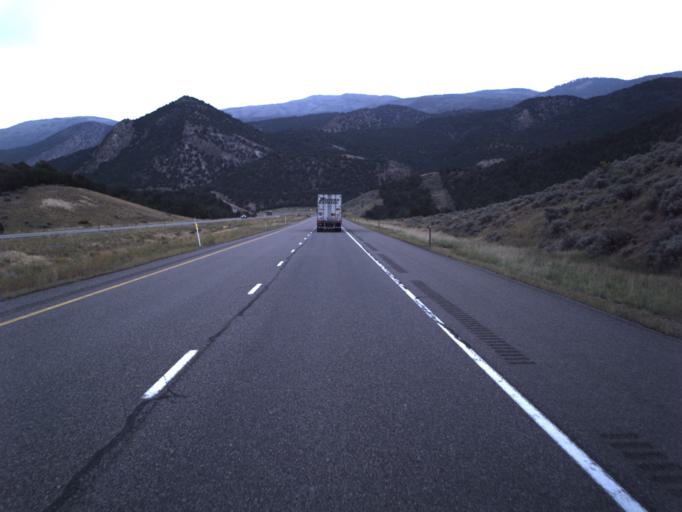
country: US
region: Utah
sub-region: Sevier County
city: Monroe
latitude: 38.5497
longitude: -112.3865
